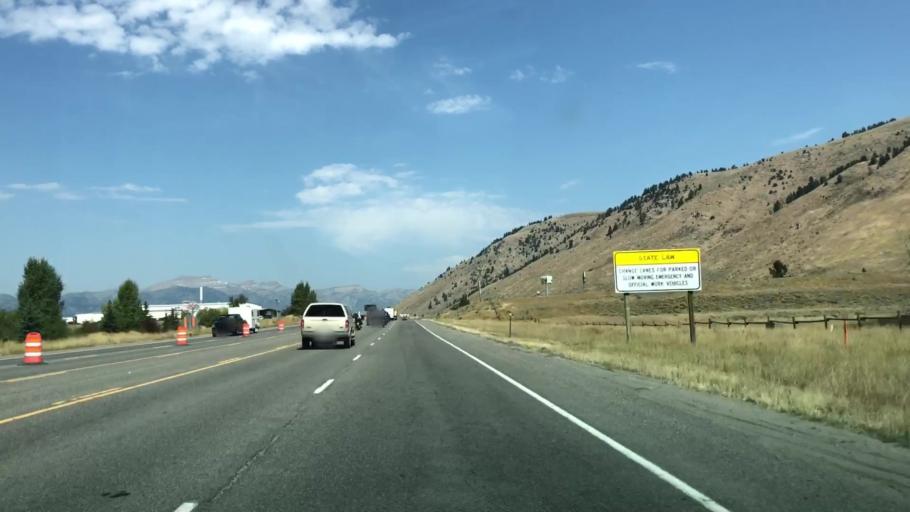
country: US
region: Wyoming
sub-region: Teton County
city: South Park
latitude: 43.4160
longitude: -110.7736
